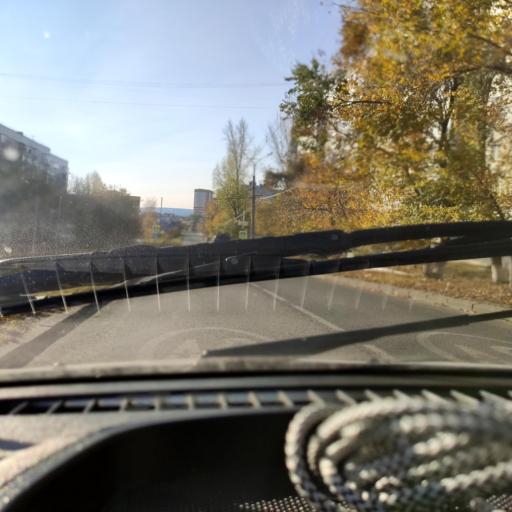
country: RU
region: Samara
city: Zhigulevsk
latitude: 53.4791
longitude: 49.4736
